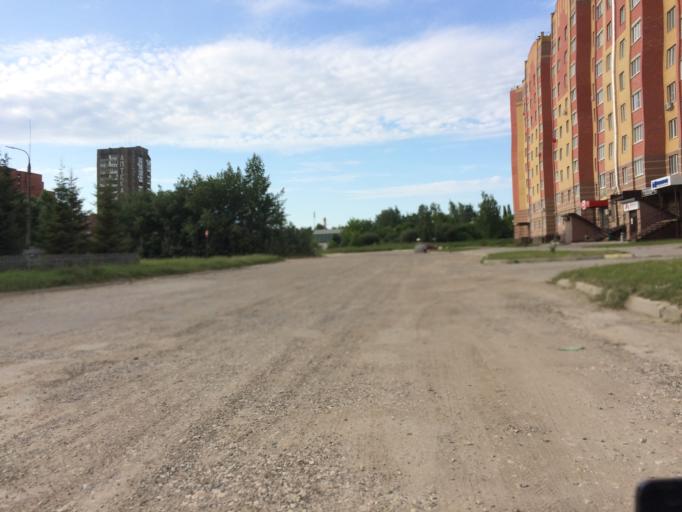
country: RU
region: Mariy-El
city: Yoshkar-Ola
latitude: 56.6431
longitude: 47.8571
